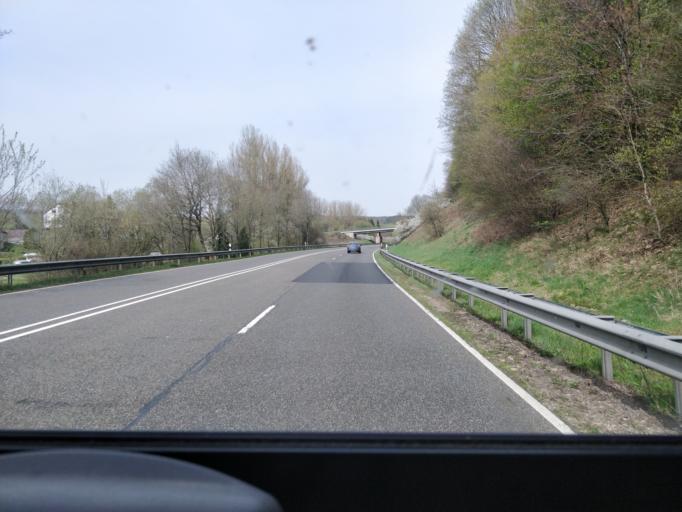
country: DE
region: Rheinland-Pfalz
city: Neuendorf
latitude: 50.2804
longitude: 6.4604
